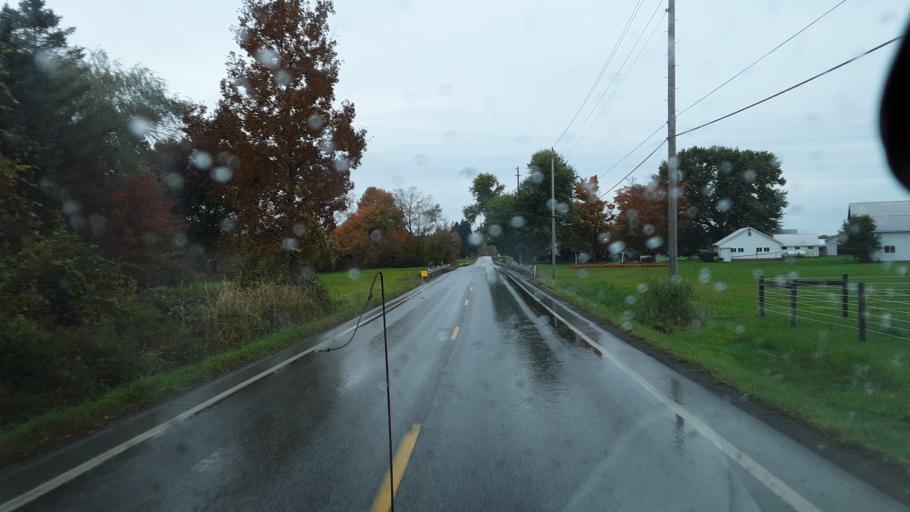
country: US
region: Ohio
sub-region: Geauga County
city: Middlefield
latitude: 41.4292
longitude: -81.1077
